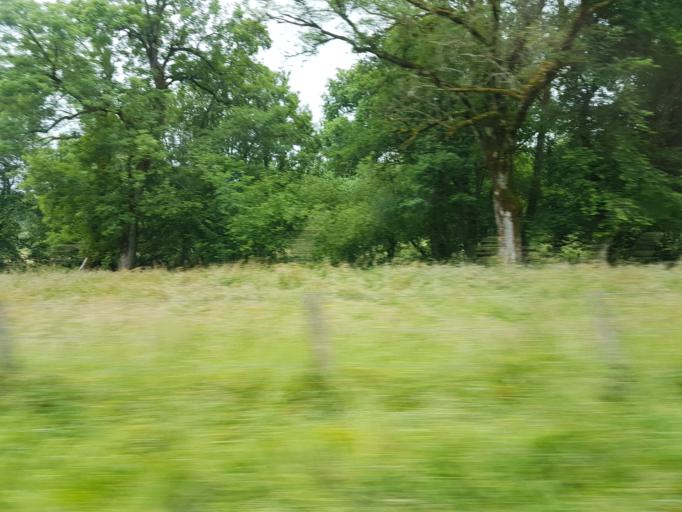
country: FR
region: Bourgogne
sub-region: Departement de la Nievre
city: Lormes
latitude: 47.1722
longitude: 3.8363
